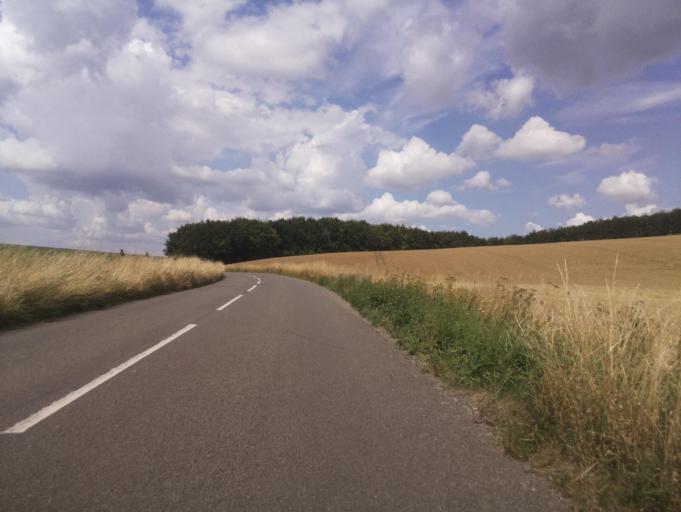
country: GB
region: England
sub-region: Borough of Swindon
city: Bishopstone
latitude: 51.5492
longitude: -1.5959
